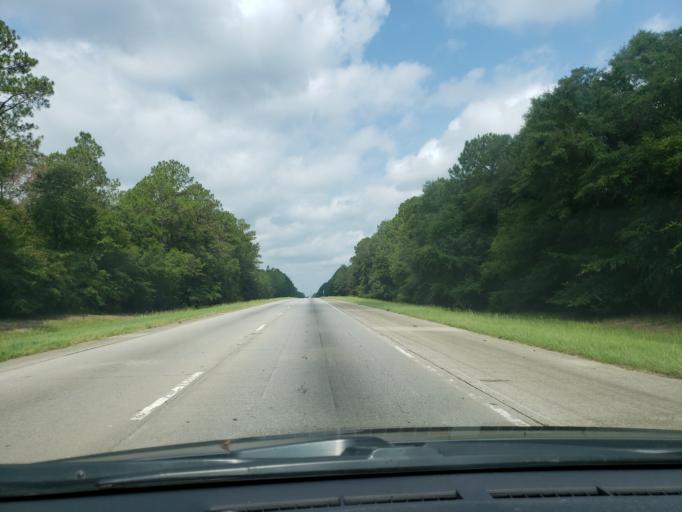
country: US
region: Georgia
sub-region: Emanuel County
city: Swainsboro
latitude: 32.4112
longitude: -82.3613
